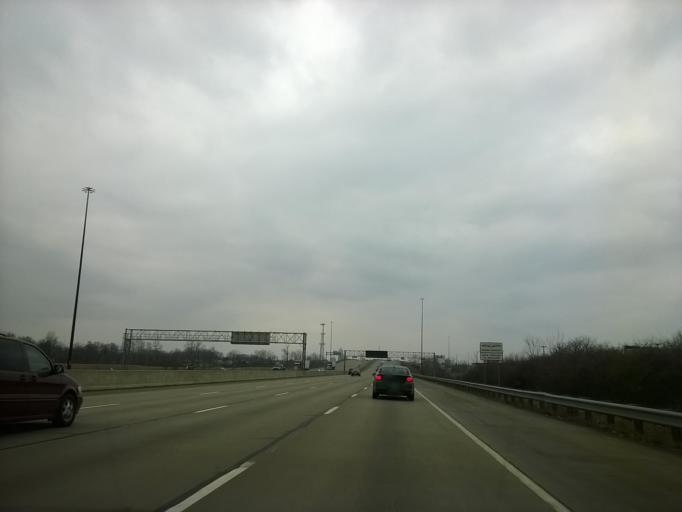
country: US
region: Indiana
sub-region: Marion County
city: Warren Park
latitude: 39.8005
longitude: -86.0946
